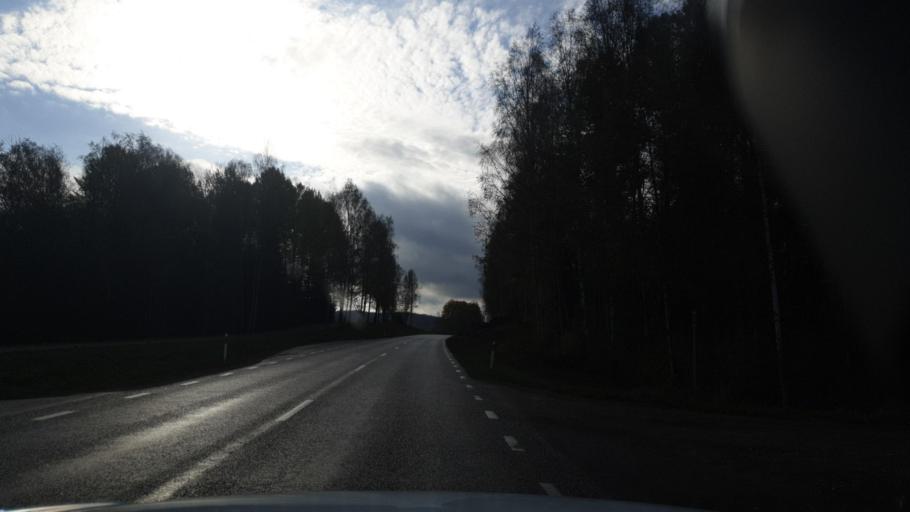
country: SE
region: Vaermland
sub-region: Arvika Kommun
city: Arvika
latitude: 59.4766
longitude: 12.7706
